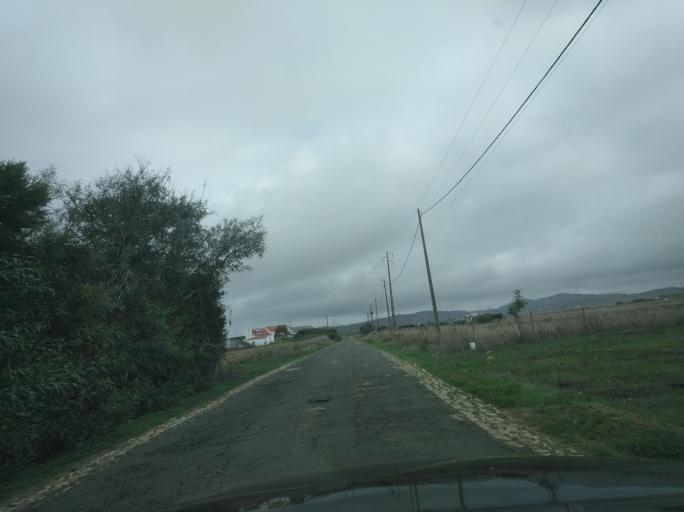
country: PT
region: Setubal
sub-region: Sines
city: Porto Covo
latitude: 37.8436
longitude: -8.7763
